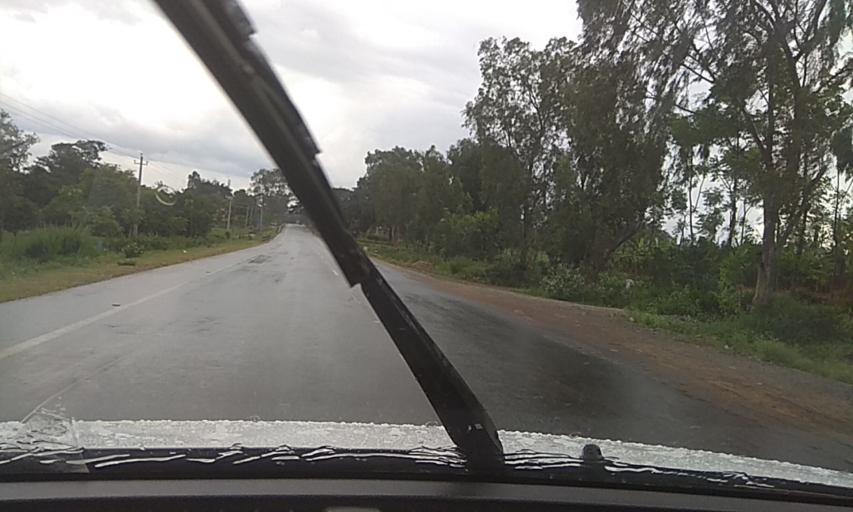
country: IN
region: Karnataka
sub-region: Tumkur
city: Kunigal
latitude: 12.9447
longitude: 77.0278
